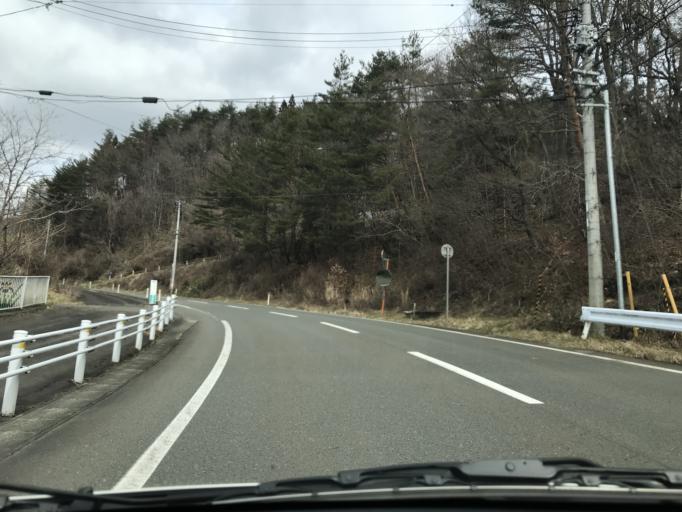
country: JP
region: Iwate
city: Tono
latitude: 39.2921
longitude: 141.3314
